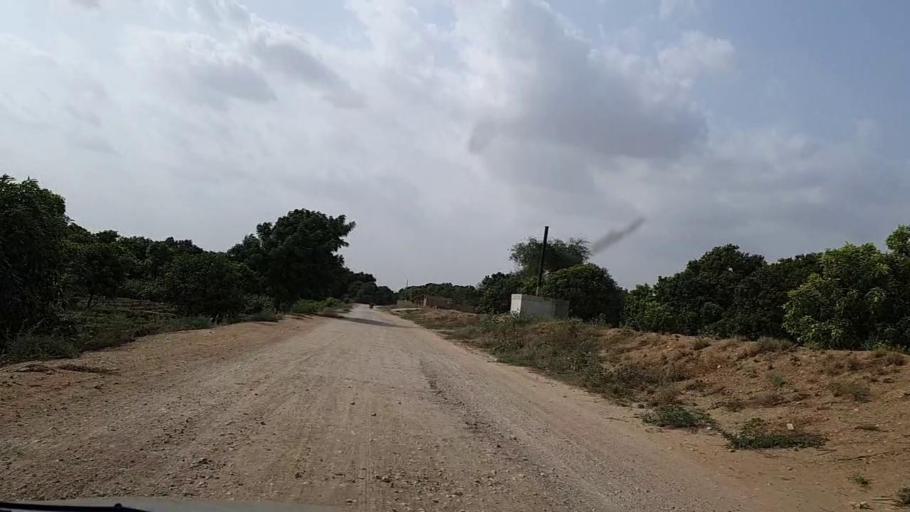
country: PK
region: Sindh
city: Kotri
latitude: 25.2477
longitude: 68.2604
